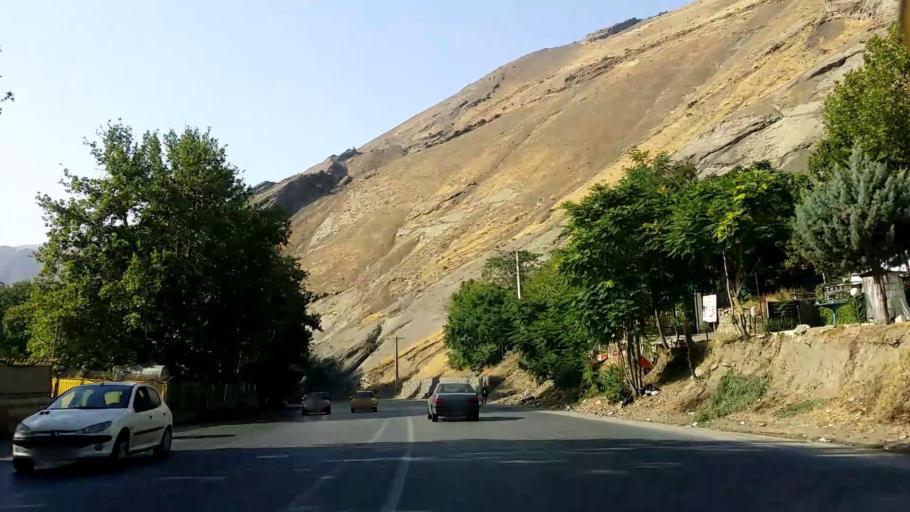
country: IR
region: Alborz
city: Karaj
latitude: 35.8641
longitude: 51.0531
